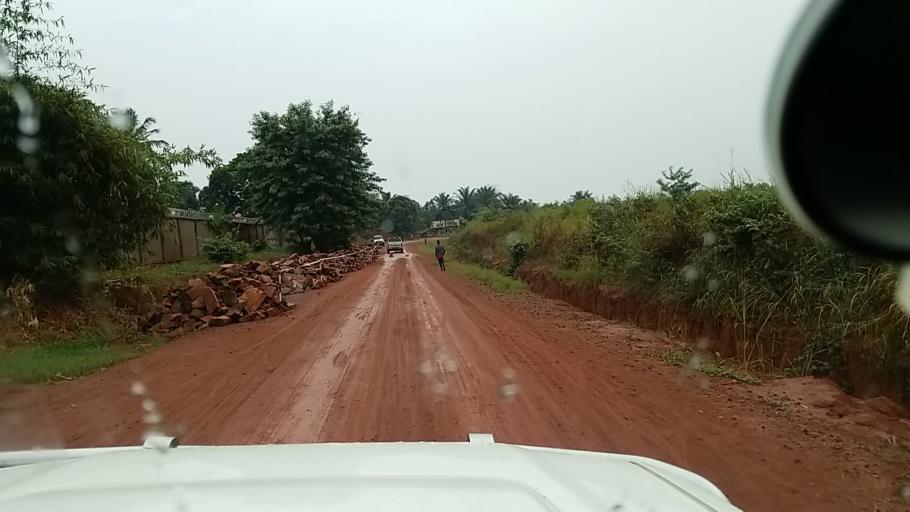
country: CD
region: Equateur
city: Gemena
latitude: 3.2347
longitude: 19.7804
